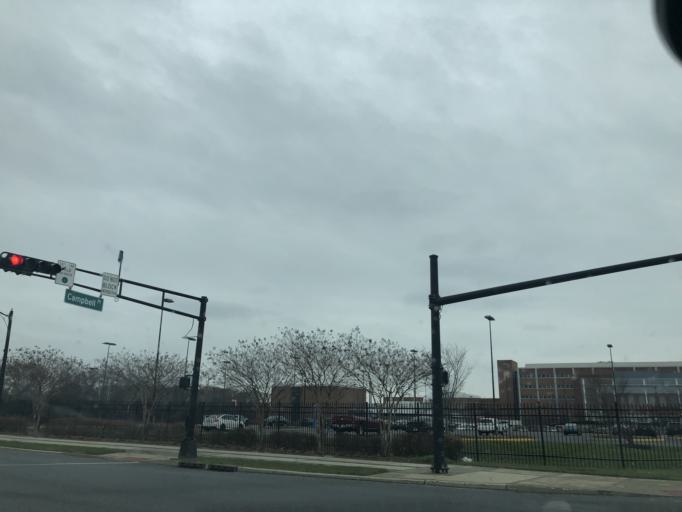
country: US
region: New Jersey
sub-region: Camden County
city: Camden
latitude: 39.9412
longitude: -75.1080
